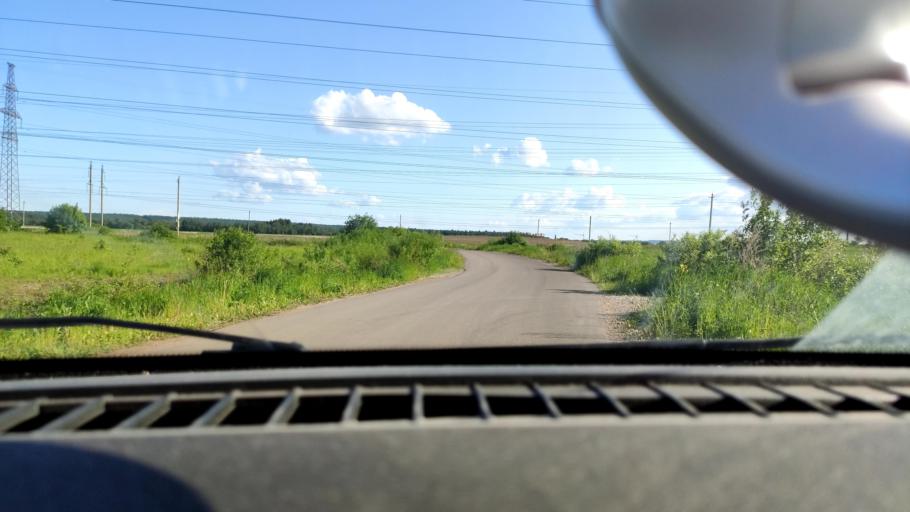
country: RU
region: Perm
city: Ferma
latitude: 57.9166
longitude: 56.3390
